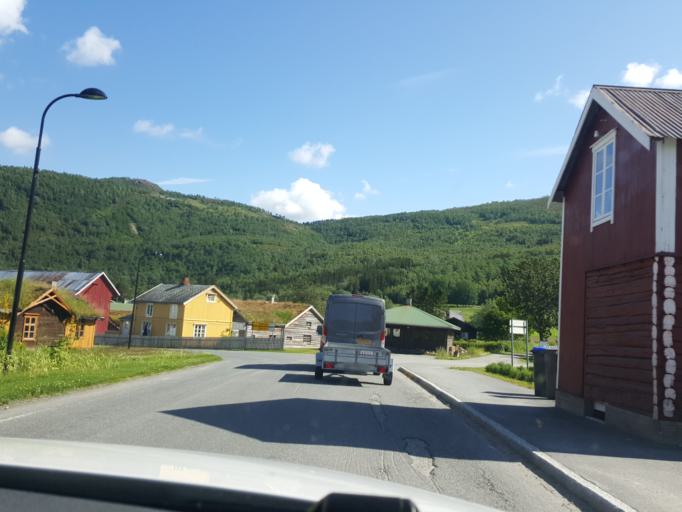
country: NO
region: Nordland
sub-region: Bodo
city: Loding
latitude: 67.1162
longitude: 15.0084
